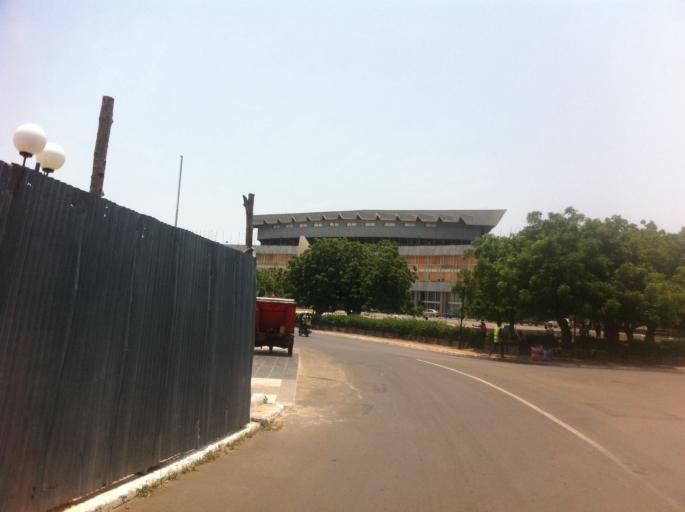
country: TG
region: Maritime
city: Lome
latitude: 6.1294
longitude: 1.2164
